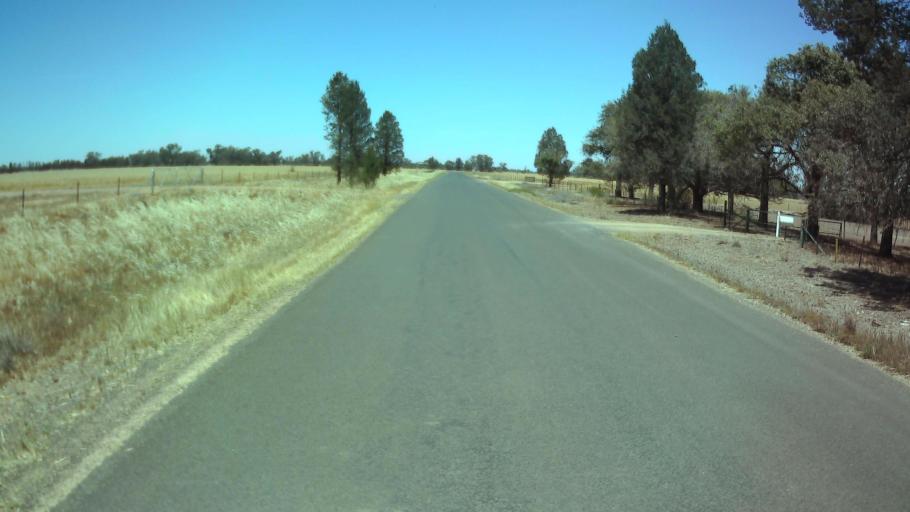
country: AU
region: New South Wales
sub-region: Weddin
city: Grenfell
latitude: -34.0317
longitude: 147.7905
